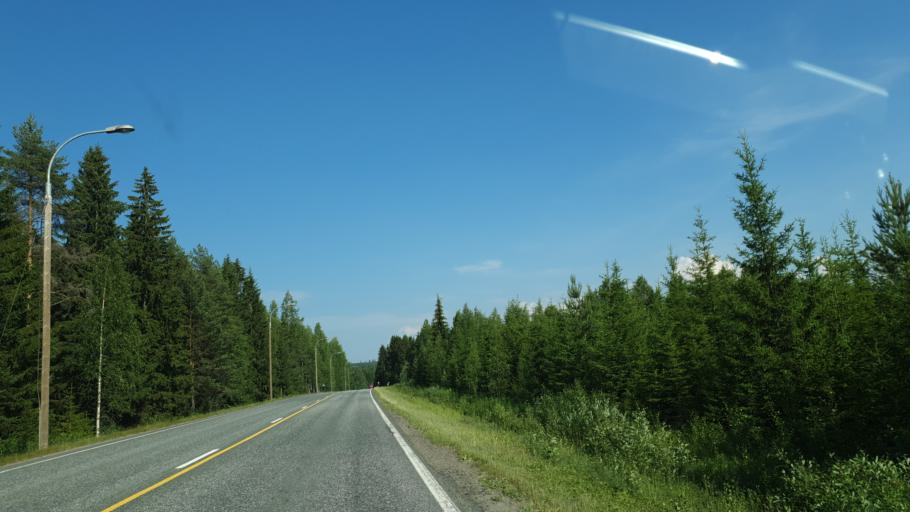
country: FI
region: Northern Savo
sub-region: Kuopio
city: Nilsiae
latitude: 63.1415
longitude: 27.9222
